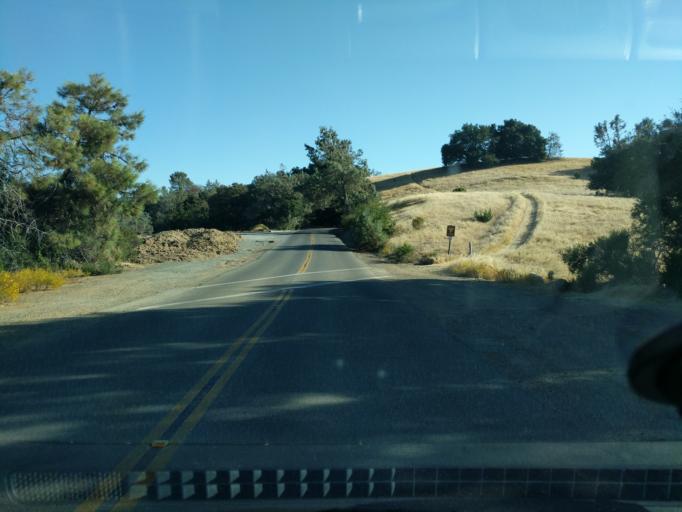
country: US
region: California
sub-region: Contra Costa County
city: Diablo
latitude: 37.8586
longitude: -121.9355
